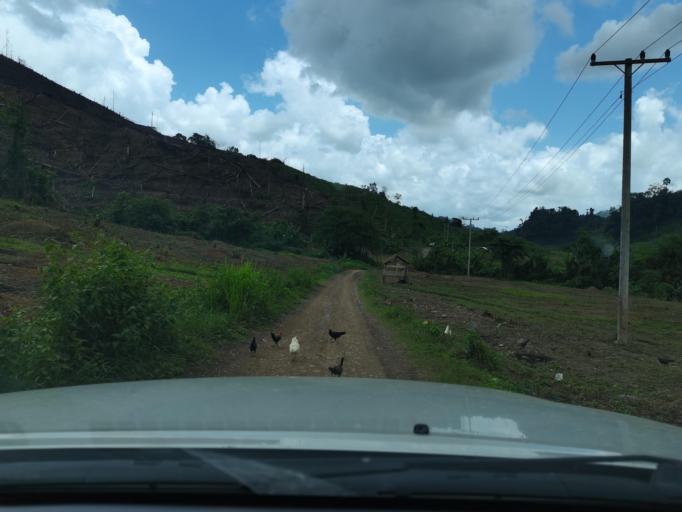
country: LA
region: Loungnamtha
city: Muang Long
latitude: 20.7656
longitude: 101.0176
